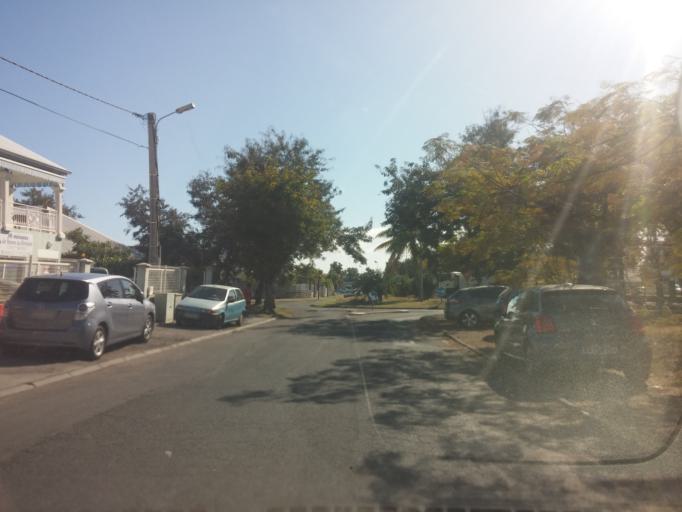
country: RE
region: Reunion
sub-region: Reunion
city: Le Port
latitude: -20.9371
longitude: 55.2986
